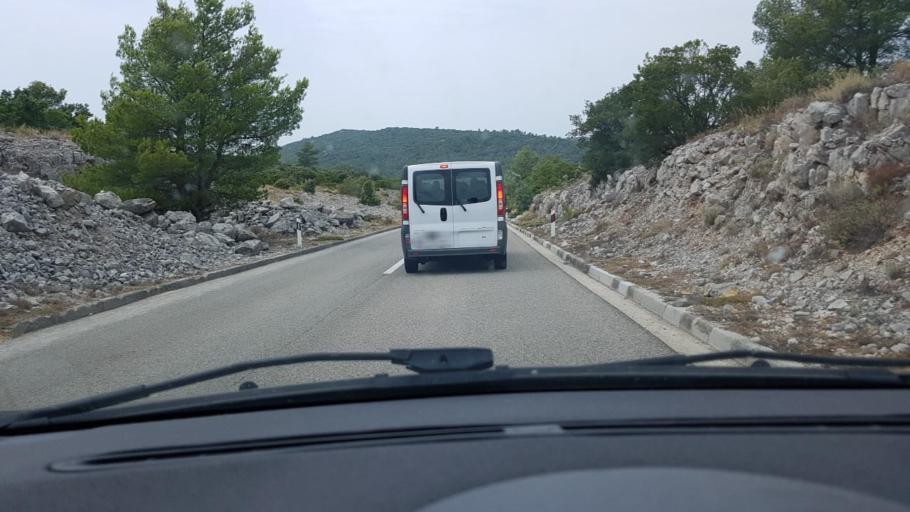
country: HR
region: Dubrovacko-Neretvanska
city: Smokvica
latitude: 42.9492
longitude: 16.9743
